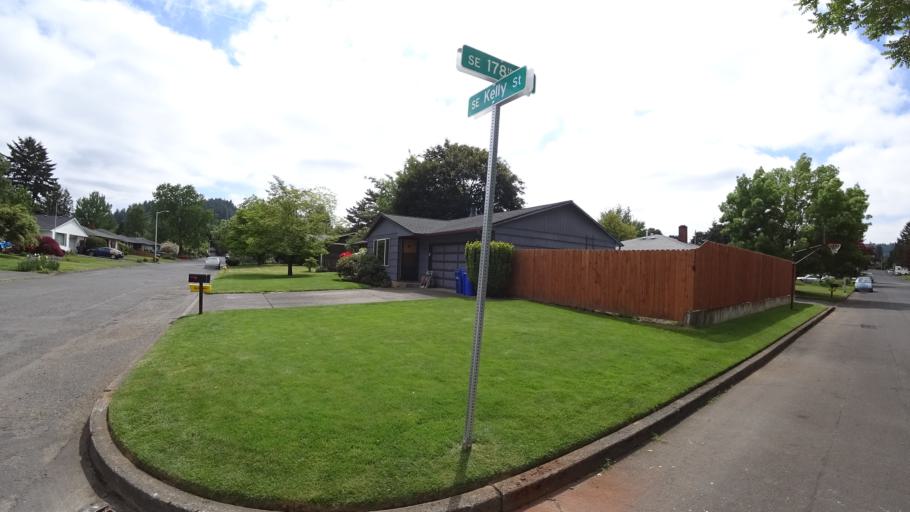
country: US
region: Oregon
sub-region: Multnomah County
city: Gresham
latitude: 45.4999
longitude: -122.4794
